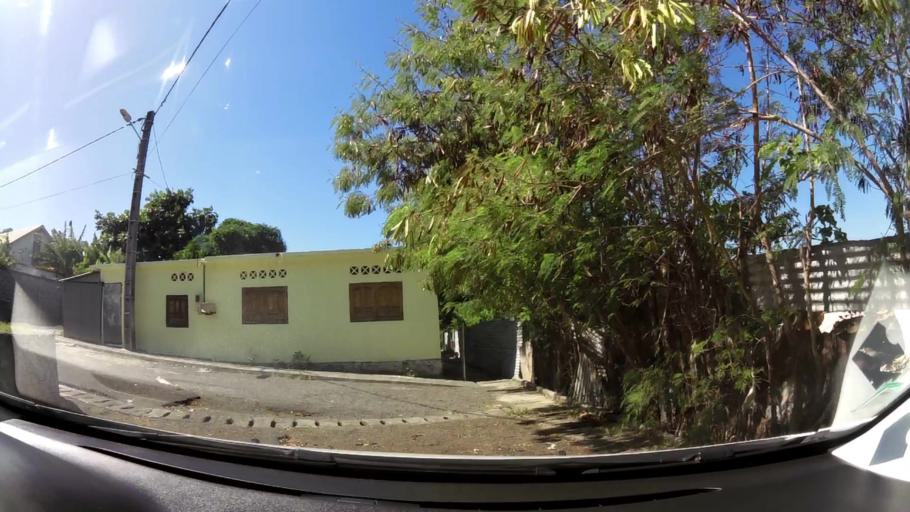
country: YT
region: Pamandzi
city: Pamandzi
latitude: -12.7993
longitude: 45.2830
